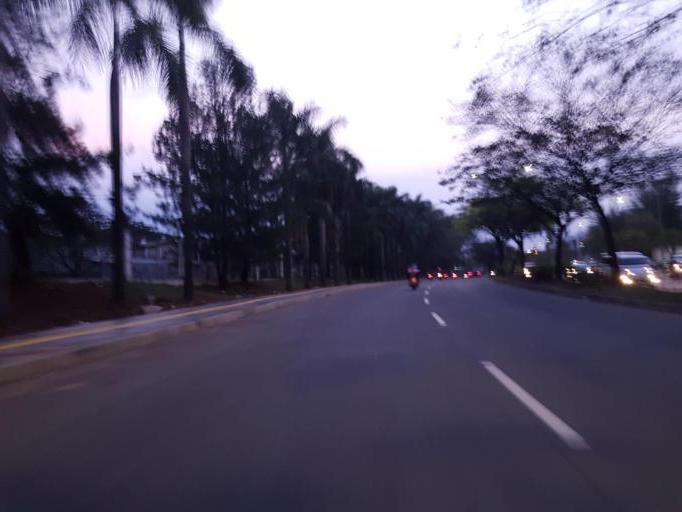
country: ID
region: West Java
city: Serpong
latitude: -6.3312
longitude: 106.6798
